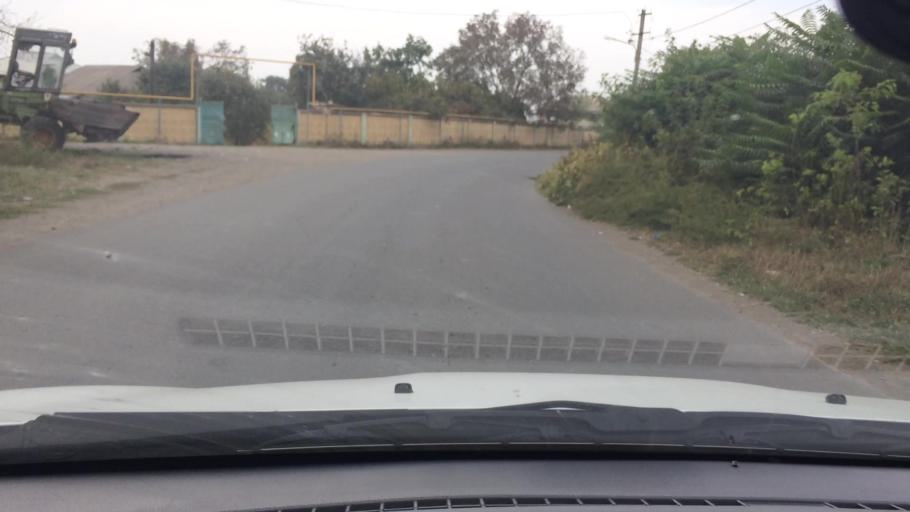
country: GE
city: Naghvarevi
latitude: 41.3521
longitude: 44.8632
